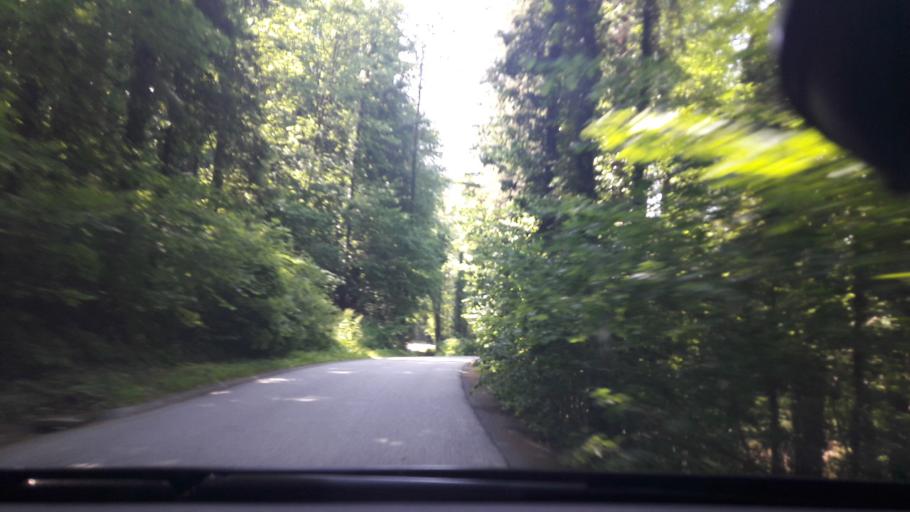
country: AT
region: Styria
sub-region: Politischer Bezirk Graz-Umgebung
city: Stiwoll
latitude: 47.1044
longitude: 15.1937
